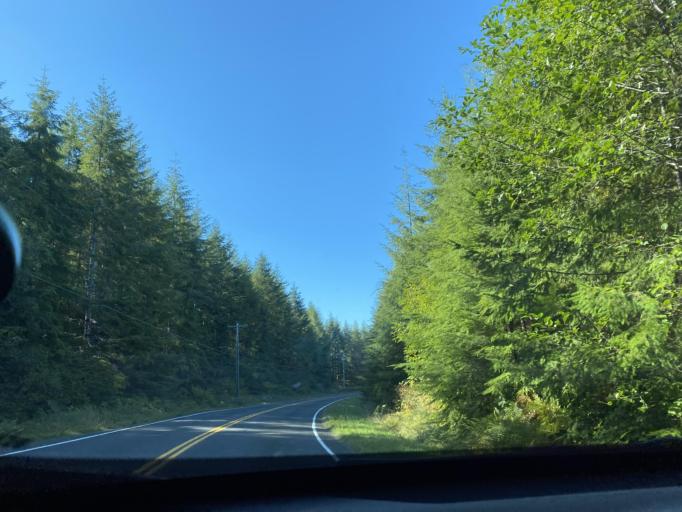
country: US
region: Washington
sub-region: Clallam County
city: Forks
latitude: 47.9483
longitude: -124.4795
